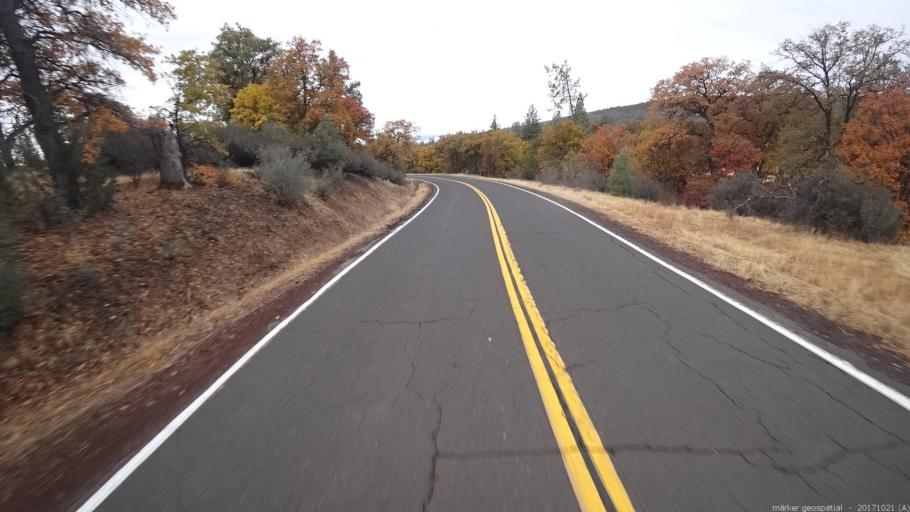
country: US
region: California
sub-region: Shasta County
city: Burney
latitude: 40.9977
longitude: -121.5032
